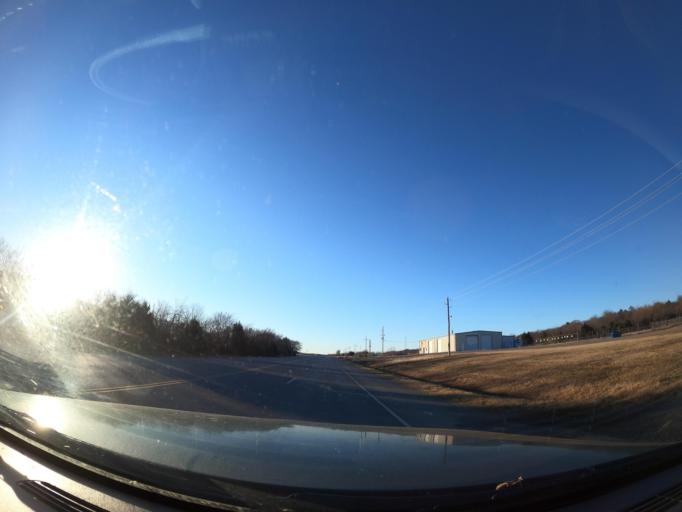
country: US
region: Oklahoma
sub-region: Pittsburg County
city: Krebs
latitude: 34.8975
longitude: -95.6781
